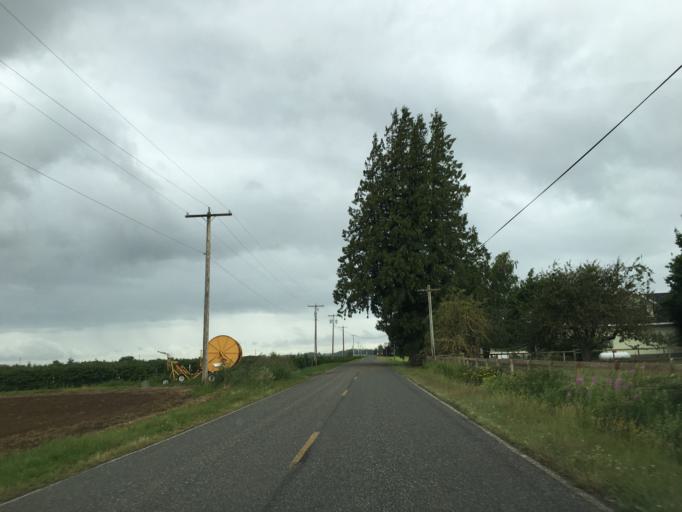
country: US
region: Washington
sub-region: Whatcom County
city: Lynden
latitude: 48.9787
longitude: -122.4177
